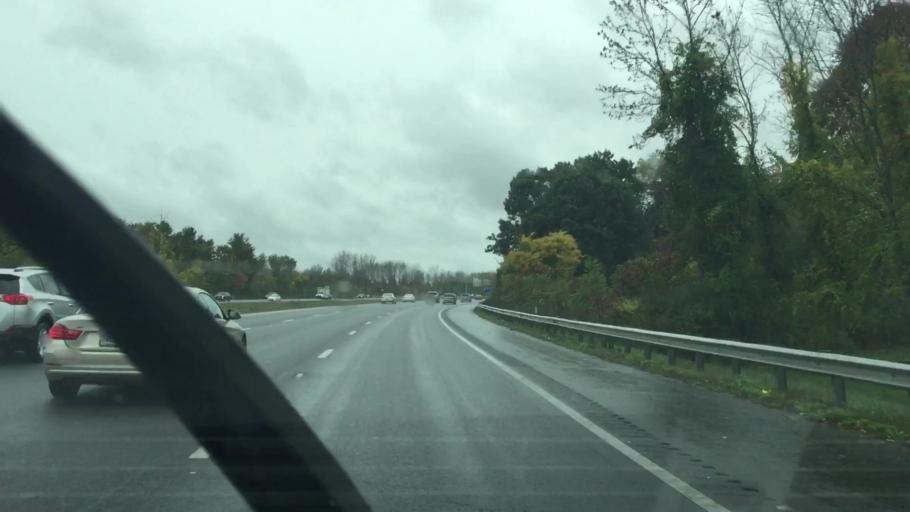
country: US
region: Massachusetts
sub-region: Essex County
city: Haverhill
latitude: 42.7599
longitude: -71.1230
